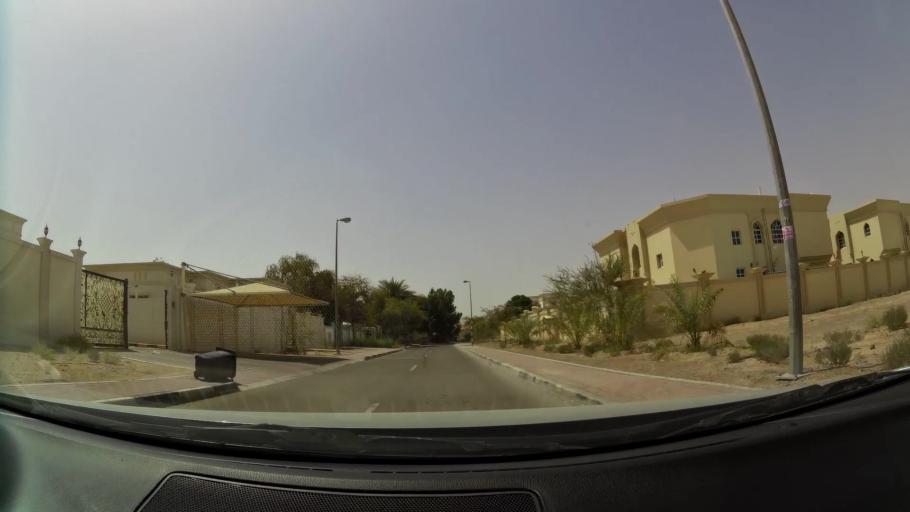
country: AE
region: Abu Dhabi
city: Al Ain
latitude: 24.1732
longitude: 55.7134
